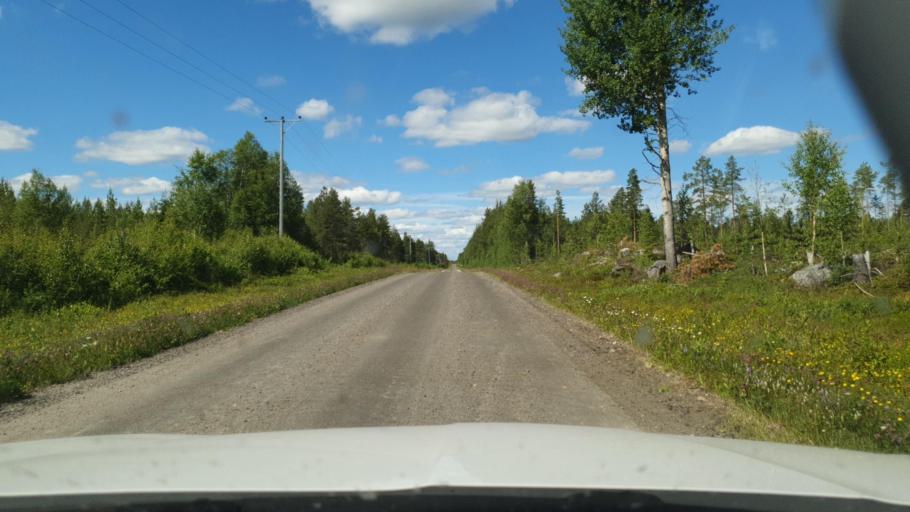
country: SE
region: Vaesterbotten
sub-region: Skelleftea Kommun
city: Backa
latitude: 65.1645
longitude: 21.1361
